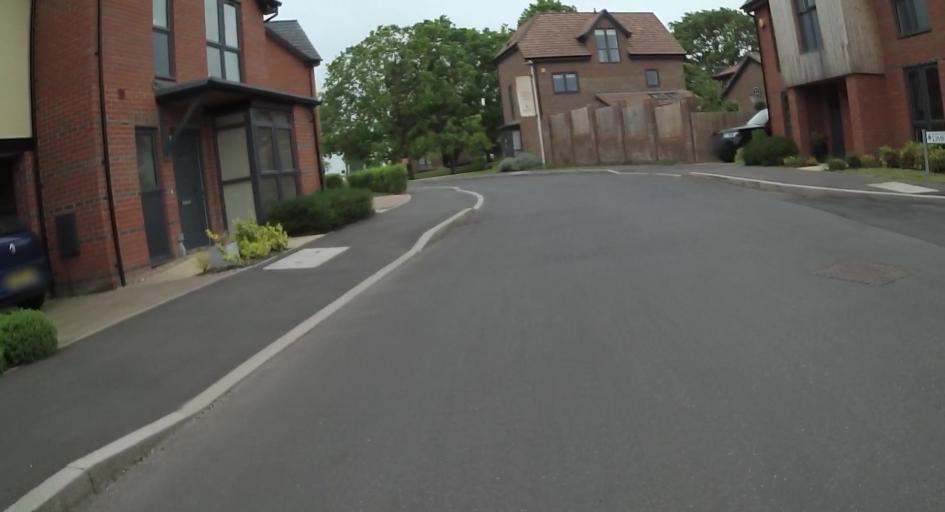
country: GB
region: England
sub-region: Wokingham
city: Barkham
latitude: 51.3863
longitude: -0.8868
